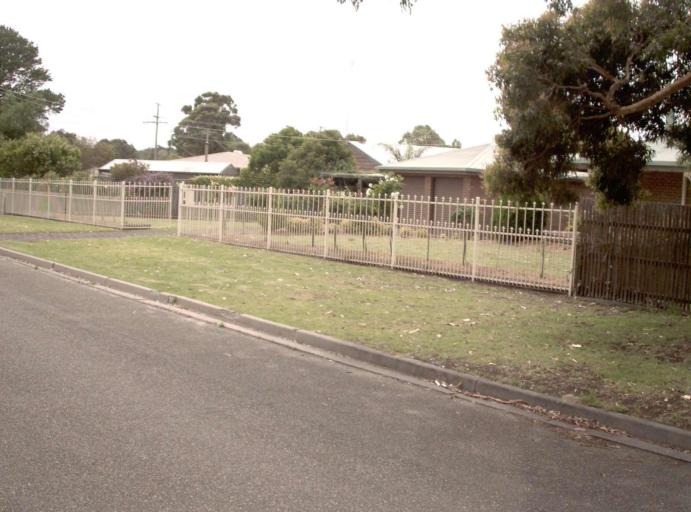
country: AU
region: Victoria
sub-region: Wellington
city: Sale
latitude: -37.9595
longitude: 147.0828
